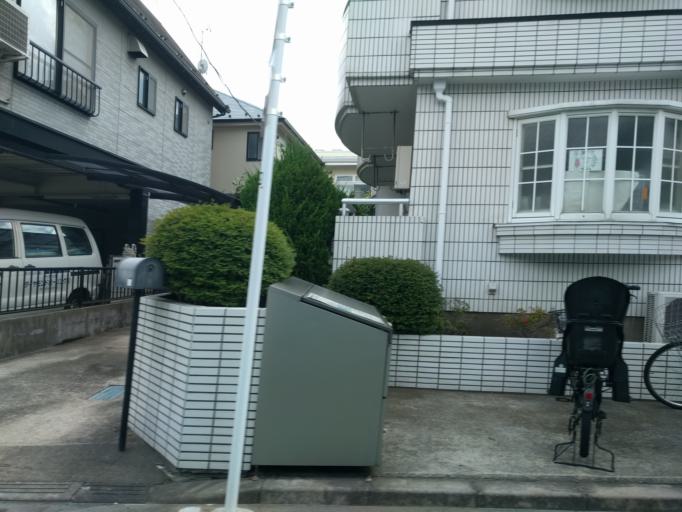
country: JP
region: Tokyo
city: Chofugaoka
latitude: 35.6371
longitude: 139.5706
